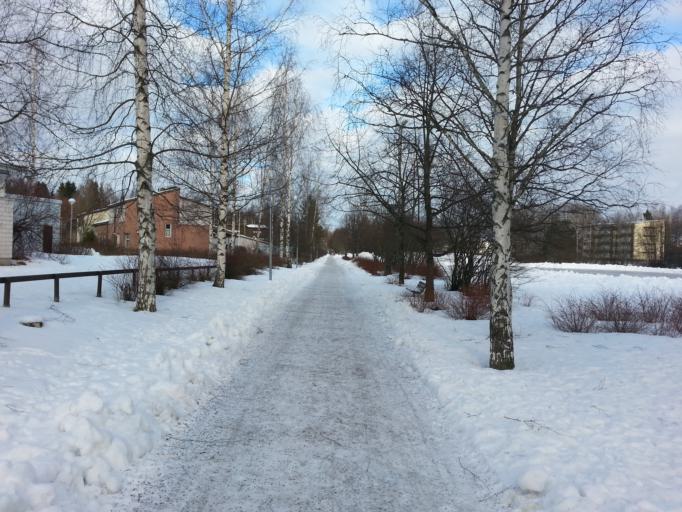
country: FI
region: Uusimaa
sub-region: Helsinki
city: Teekkarikylae
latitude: 60.2372
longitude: 24.8389
